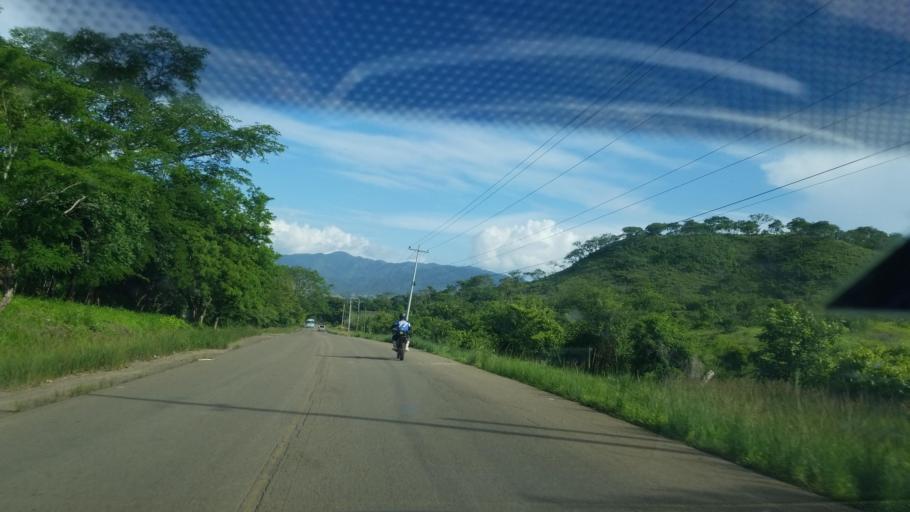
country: HN
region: El Paraiso
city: Cuyali
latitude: 13.9162
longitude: -86.5574
